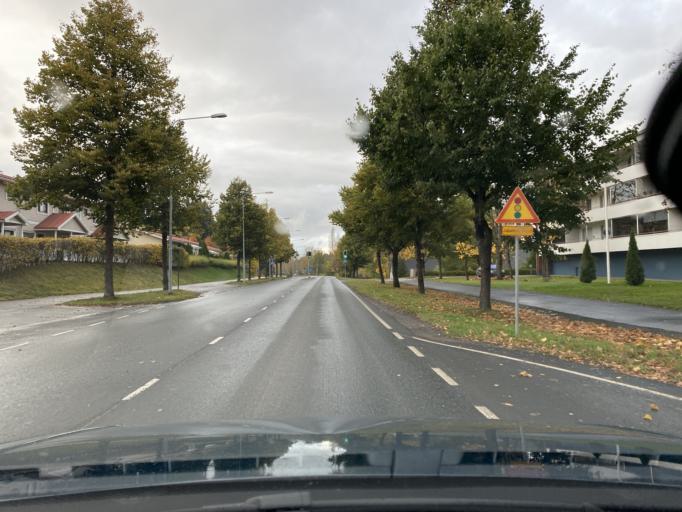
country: FI
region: Haeme
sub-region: Forssa
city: Forssa
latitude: 60.8204
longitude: 23.6079
